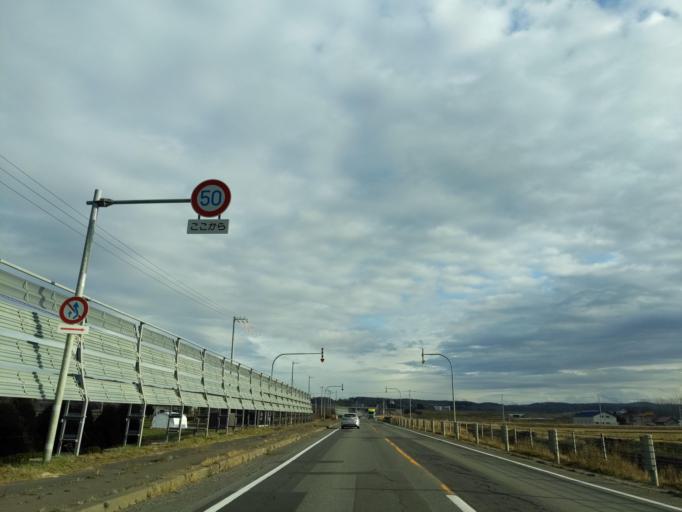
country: JP
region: Hokkaido
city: Kitahiroshima
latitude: 42.9548
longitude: 141.7050
